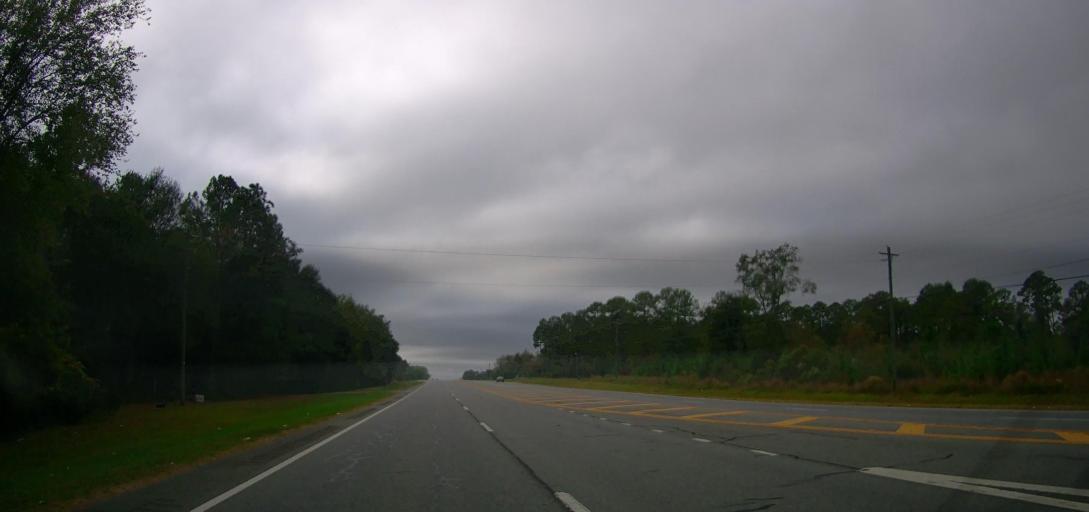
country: US
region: Georgia
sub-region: Tift County
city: Omega
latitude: 31.2937
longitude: -83.6657
